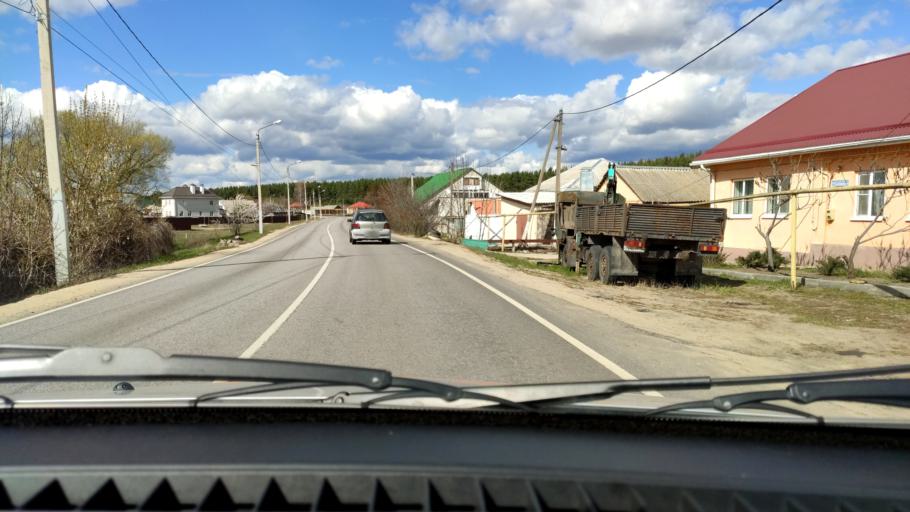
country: RU
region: Voronezj
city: Shilovo
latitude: 51.5781
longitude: 39.0376
